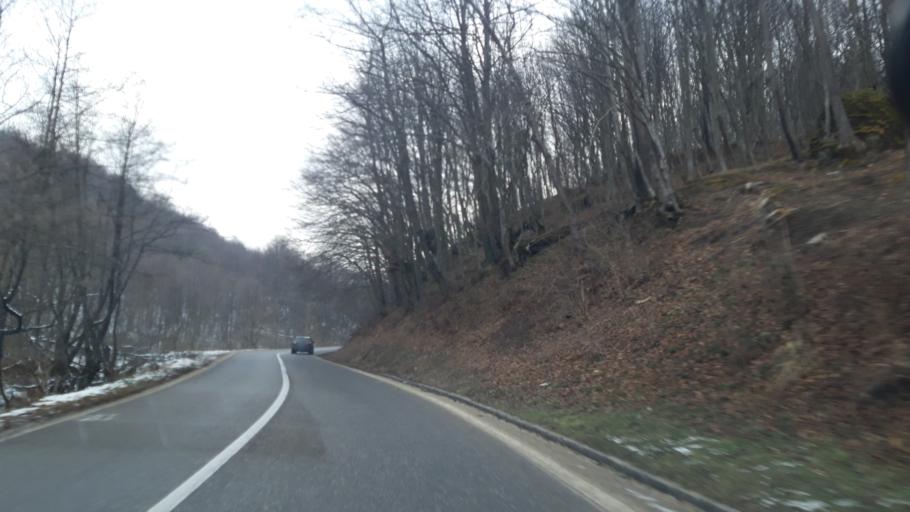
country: BA
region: Republika Srpska
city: Vlasenica
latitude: 44.1731
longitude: 19.0136
